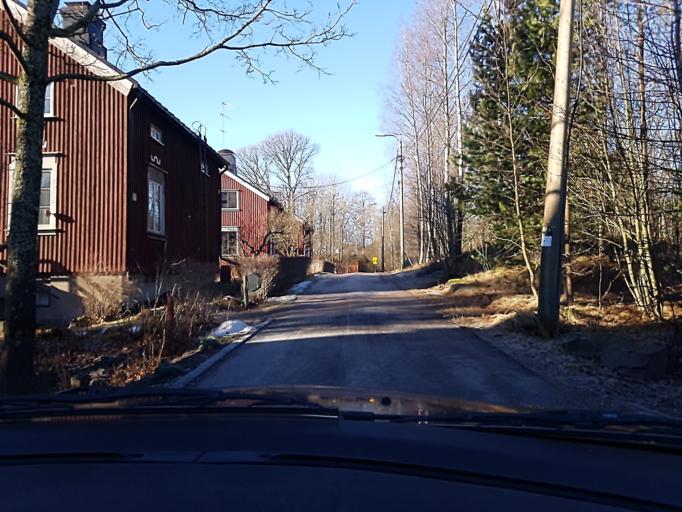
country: FI
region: Uusimaa
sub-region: Helsinki
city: Helsinki
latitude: 60.2071
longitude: 24.9577
